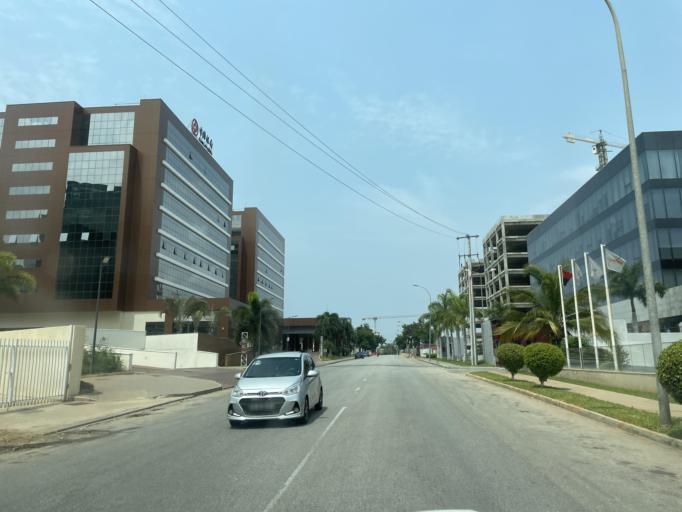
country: AO
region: Luanda
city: Luanda
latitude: -8.9242
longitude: 13.1904
